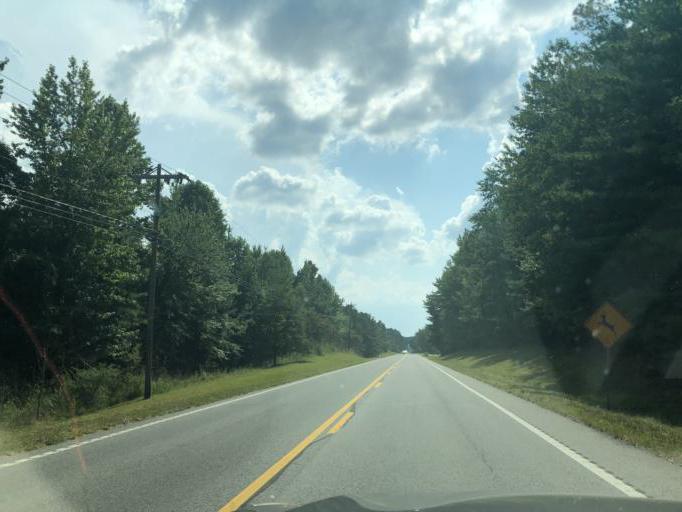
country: US
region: Tennessee
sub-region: Franklin County
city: Sewanee
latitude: 35.2164
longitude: -85.8873
